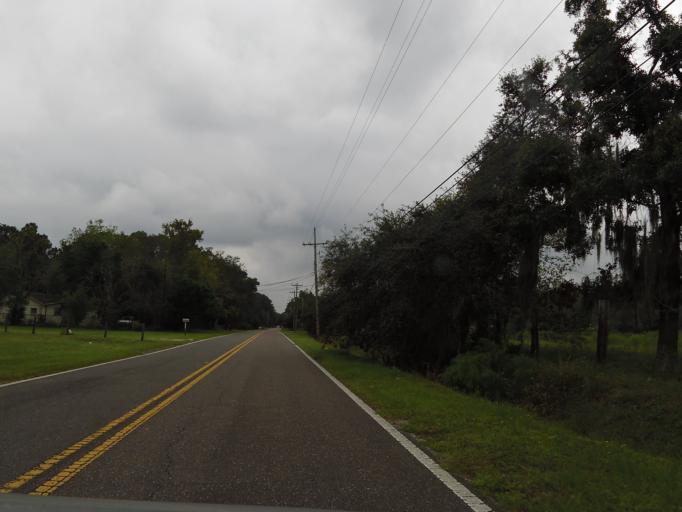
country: US
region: Florida
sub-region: Clay County
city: Bellair-Meadowbrook Terrace
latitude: 30.2198
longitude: -81.7727
